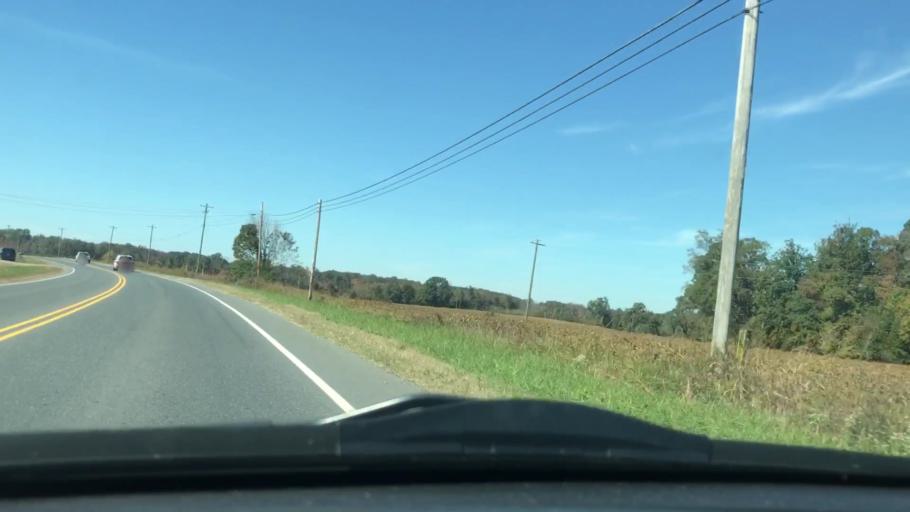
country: US
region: North Carolina
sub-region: Randolph County
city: Randleman
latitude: 35.8192
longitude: -79.8481
